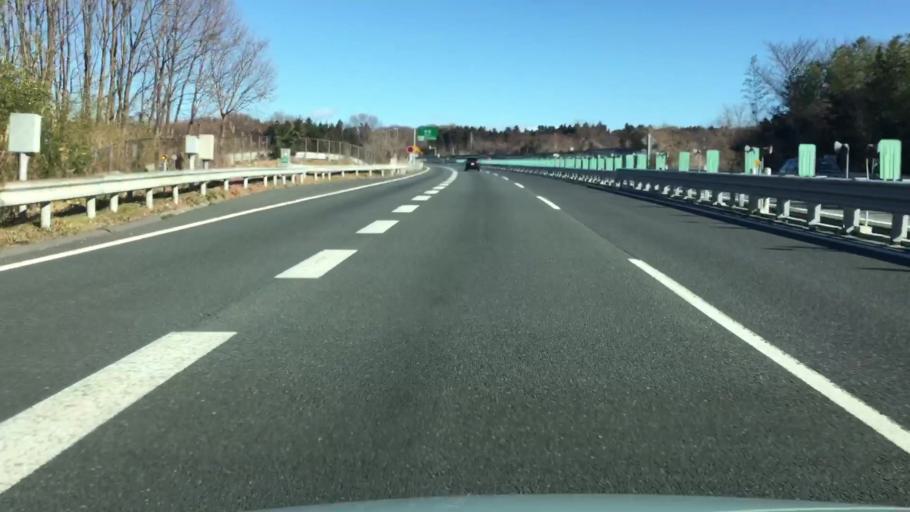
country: JP
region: Gunma
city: Shibukawa
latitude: 36.5301
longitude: 139.0445
